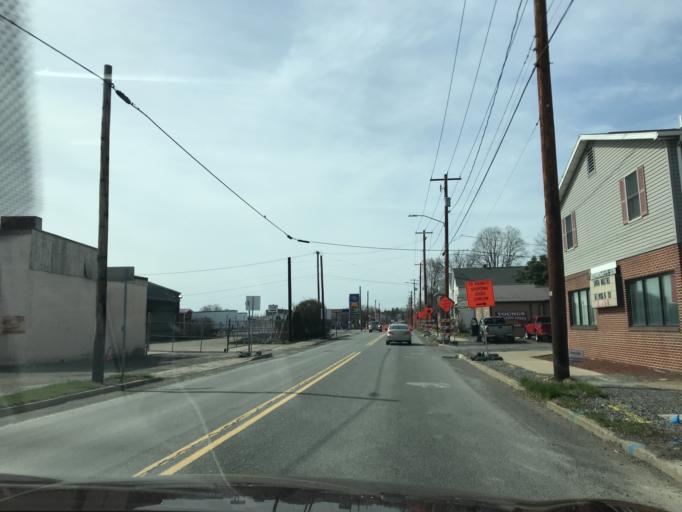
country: US
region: Pennsylvania
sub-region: Northumberland County
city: Northumberland
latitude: 40.8890
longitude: -76.7982
